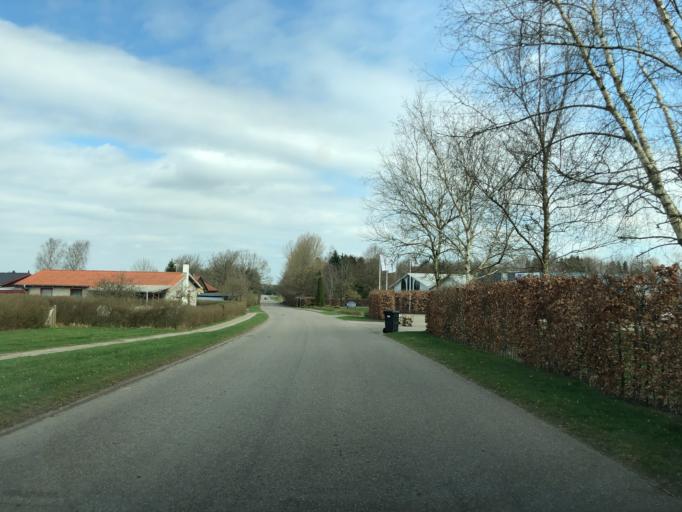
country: DK
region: South Denmark
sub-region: Vejle Kommune
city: Give
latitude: 55.9074
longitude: 9.2656
